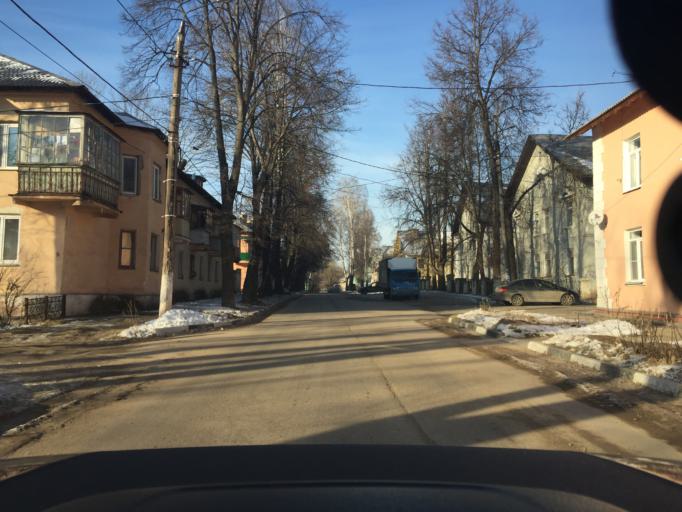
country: RU
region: Tula
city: Tula
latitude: 54.1807
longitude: 37.7078
